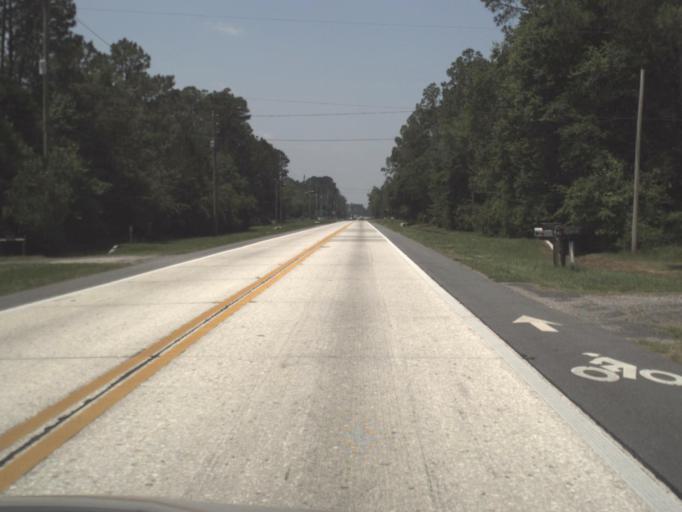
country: US
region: Florida
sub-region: Duval County
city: Baldwin
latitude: 30.2164
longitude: -81.9448
